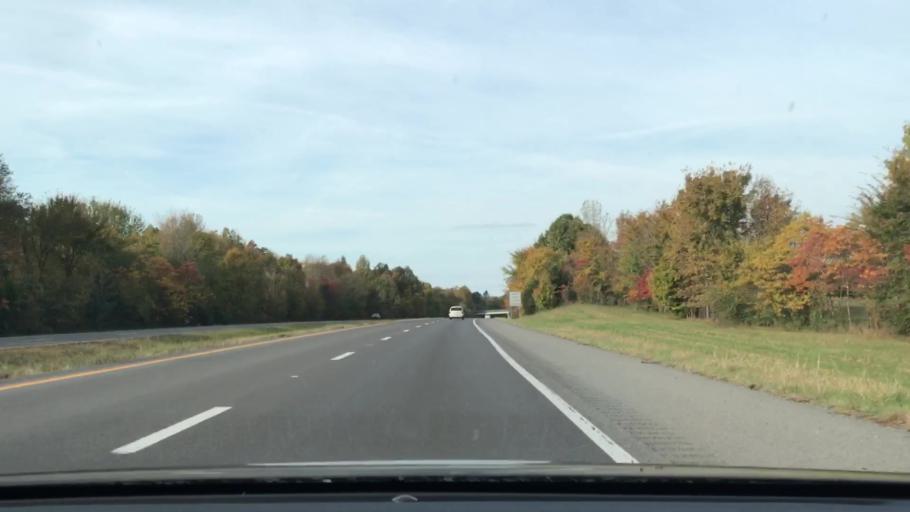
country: US
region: Kentucky
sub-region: Graves County
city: Mayfield
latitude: 36.7724
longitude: -88.6046
